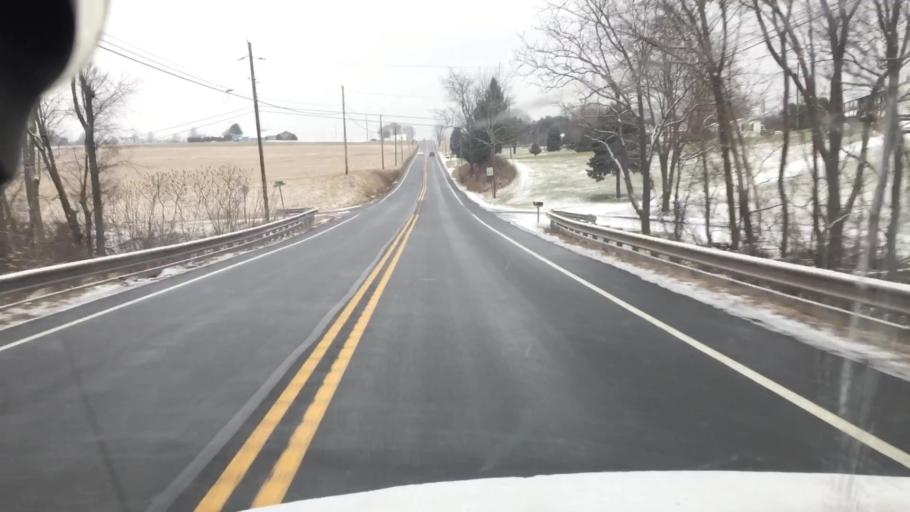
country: US
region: Pennsylvania
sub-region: Luzerne County
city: Nescopeck
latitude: 41.0366
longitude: -76.1352
